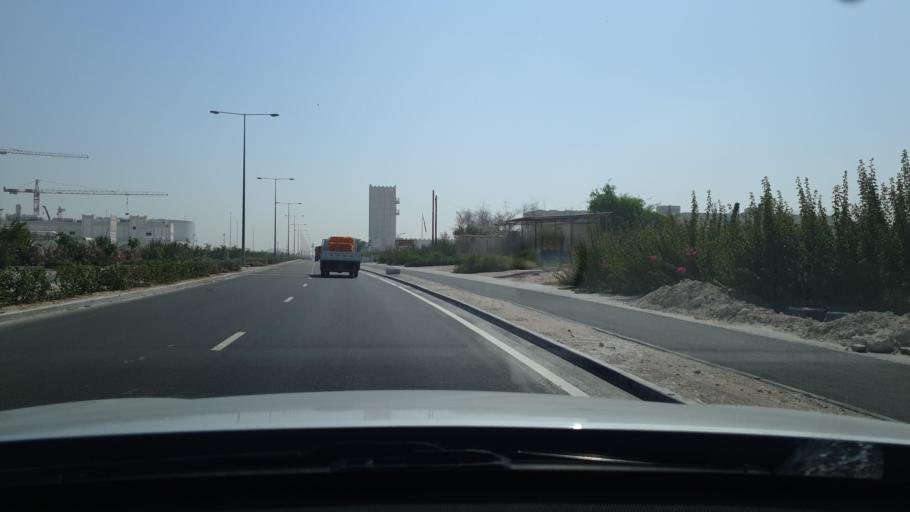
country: QA
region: Baladiyat ad Dawhah
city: Doha
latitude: 25.2333
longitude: 51.5207
